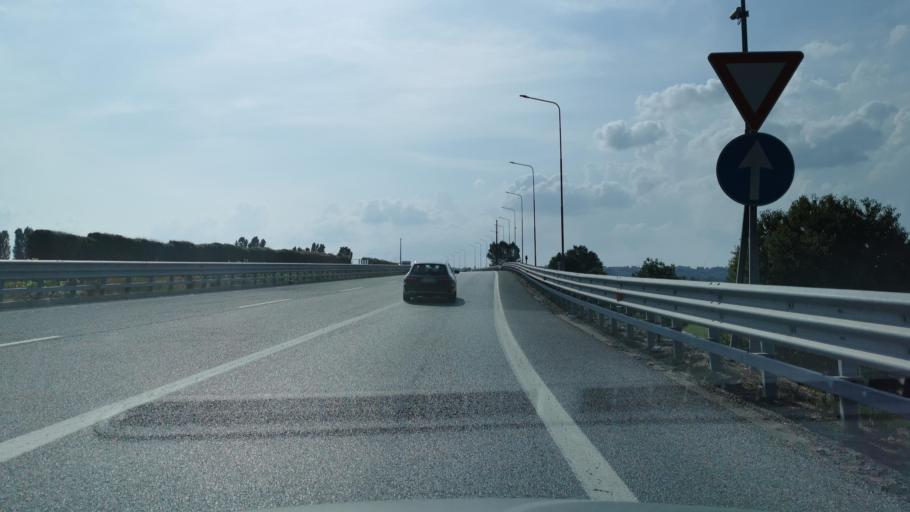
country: IT
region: Piedmont
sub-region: Provincia di Cuneo
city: Cherasco
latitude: 44.6638
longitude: 7.8745
